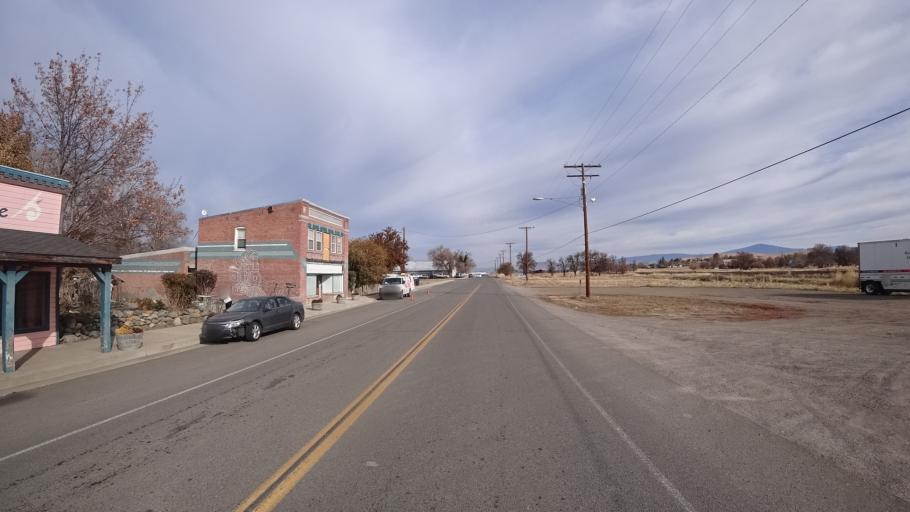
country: US
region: California
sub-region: Siskiyou County
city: Montague
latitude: 41.7284
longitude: -122.5275
